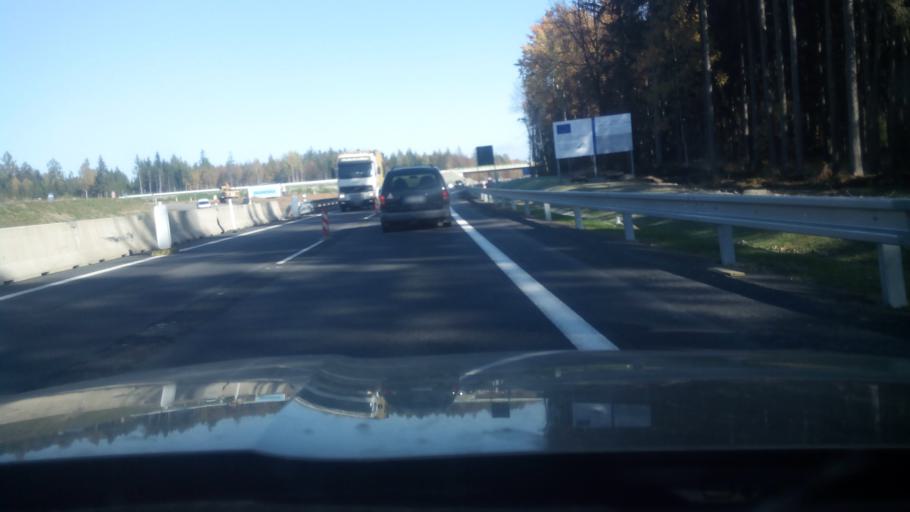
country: CZ
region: Central Bohemia
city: Milin
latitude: 49.6706
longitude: 14.0627
